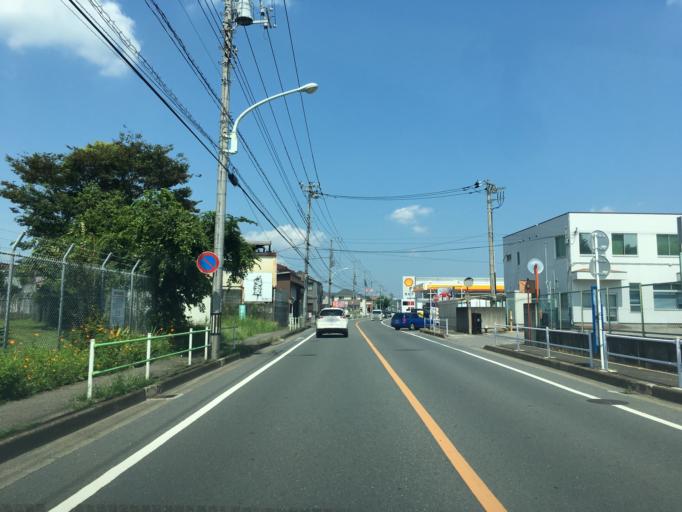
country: JP
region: Tokyo
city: Fussa
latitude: 35.7407
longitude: 139.3710
